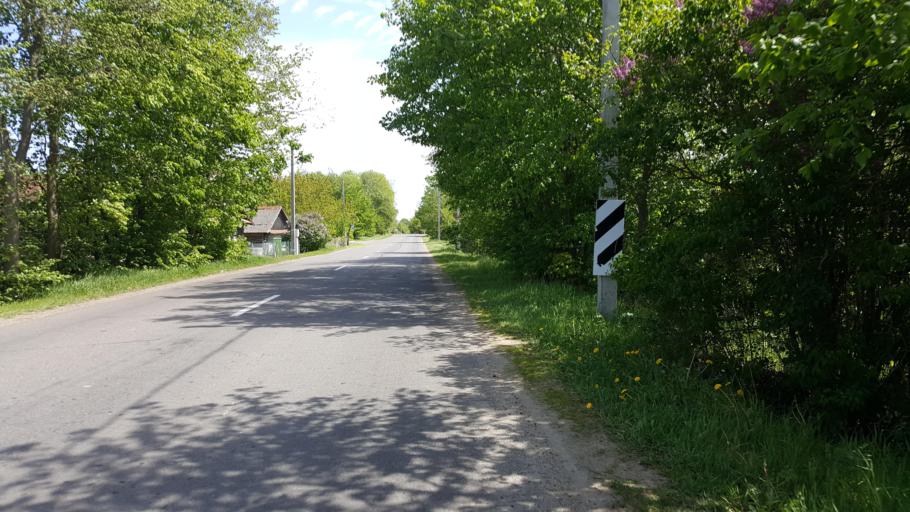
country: BY
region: Brest
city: Kobryn
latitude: 52.3469
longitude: 24.2043
